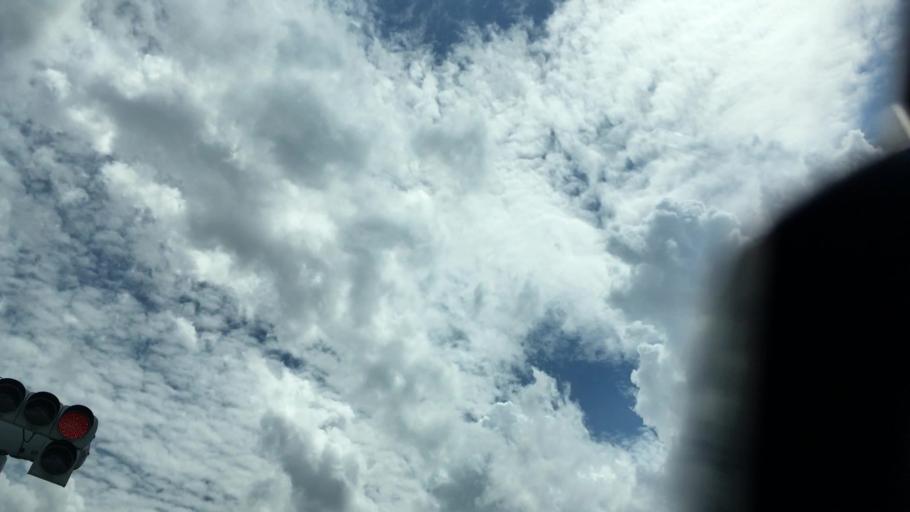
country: JP
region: Fukuoka
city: Dazaifu
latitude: 33.5083
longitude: 130.5240
